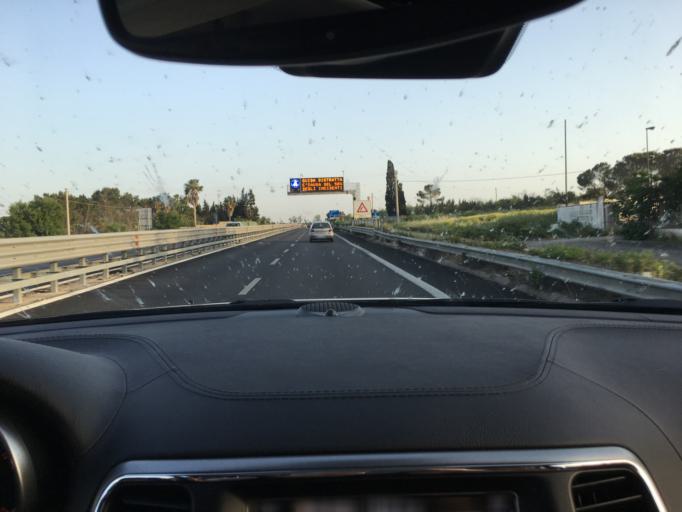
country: IT
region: Apulia
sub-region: Provincia di Lecce
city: San Pietro in Lama
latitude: 40.2944
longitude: 18.1325
